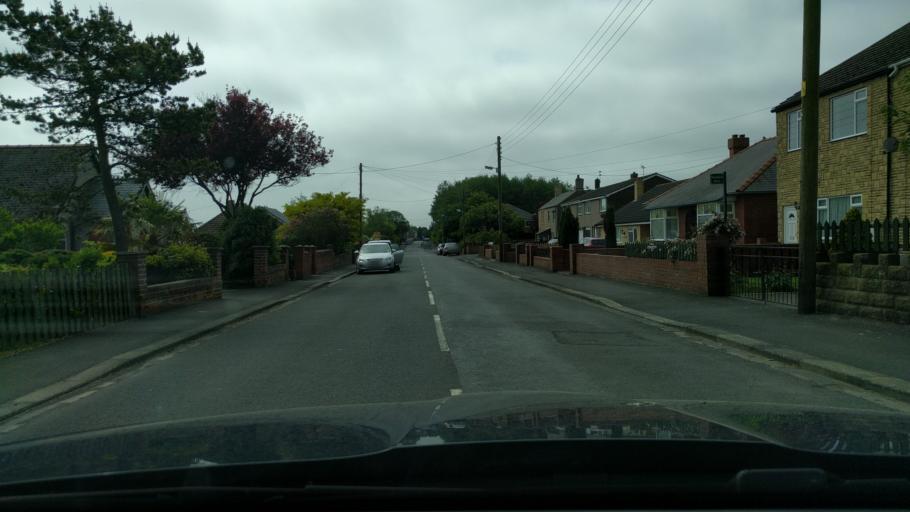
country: GB
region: England
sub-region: Northumberland
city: East Chevington
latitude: 55.2887
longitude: -1.6054
